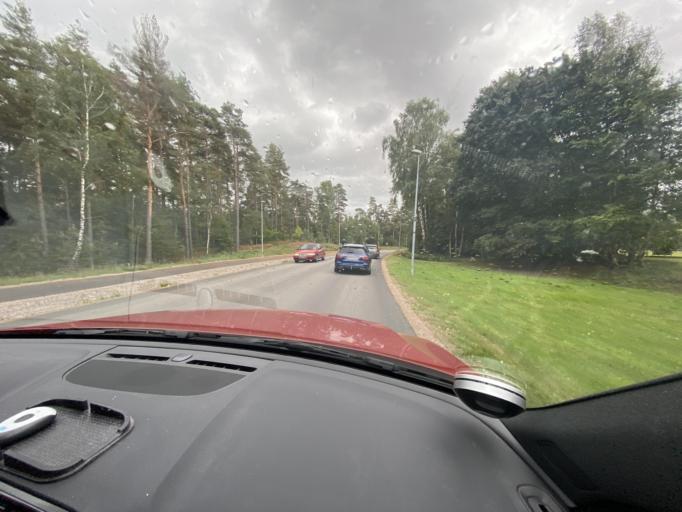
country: SE
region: Kronoberg
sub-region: Markaryds Kommun
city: Markaryd
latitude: 56.4572
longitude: 13.6185
